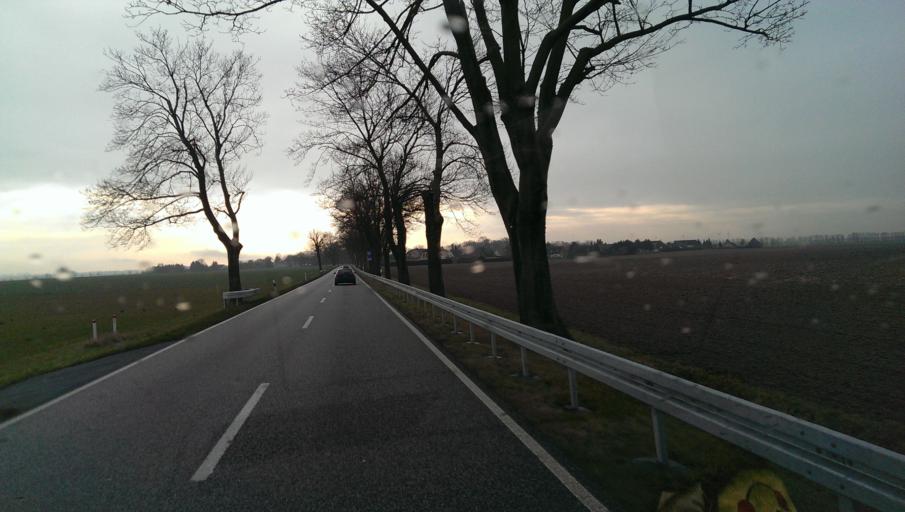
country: DE
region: Brandenburg
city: Juterbog
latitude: 51.9378
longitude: 13.1202
